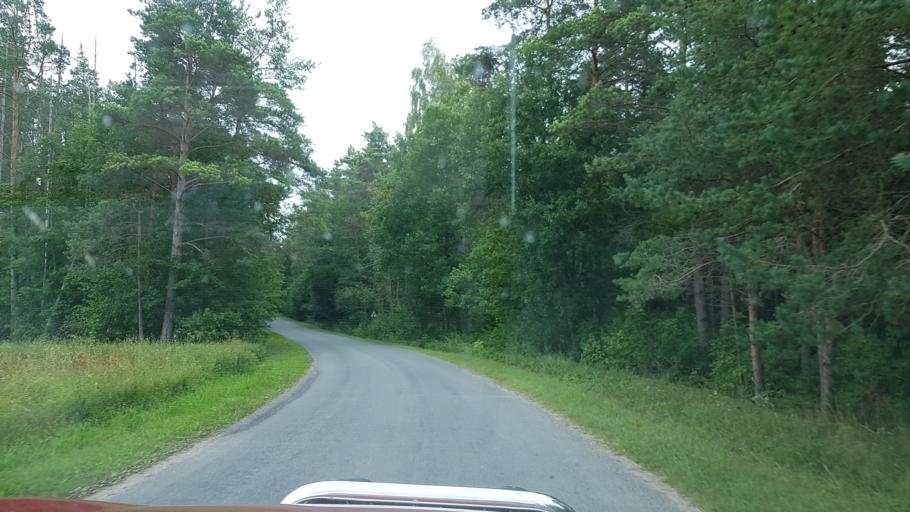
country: EE
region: Laeaene
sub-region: Ridala Parish
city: Uuemoisa
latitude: 59.0090
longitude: 23.7233
